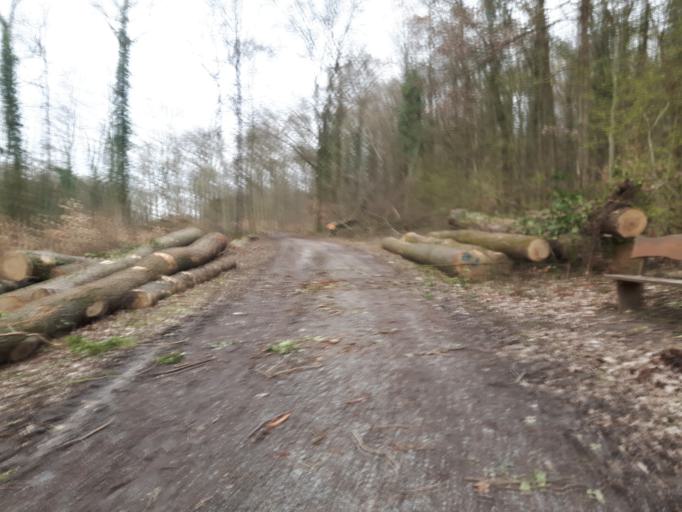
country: DE
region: Baden-Wuerttemberg
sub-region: Regierungsbezirk Stuttgart
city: Leingarten
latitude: 49.1764
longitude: 9.1564
